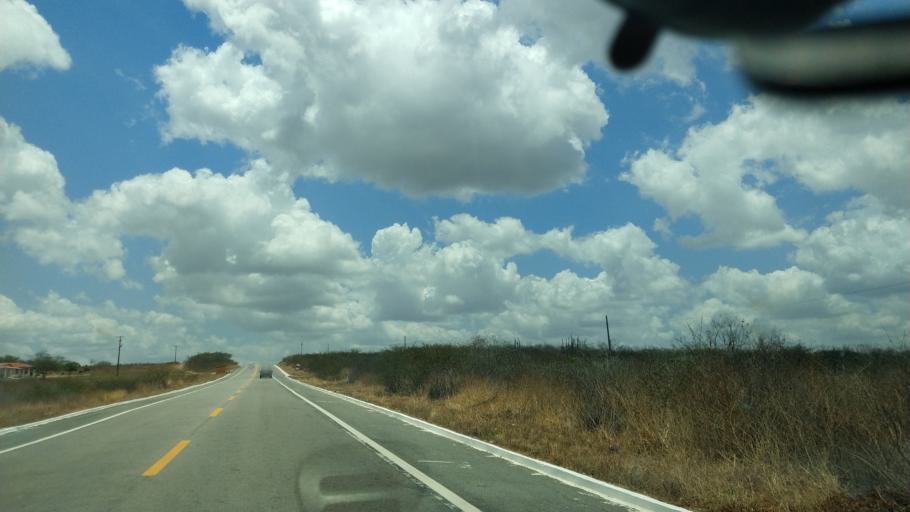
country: BR
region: Rio Grande do Norte
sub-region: Cerro Cora
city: Cerro Cora
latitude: -6.1920
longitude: -36.2172
